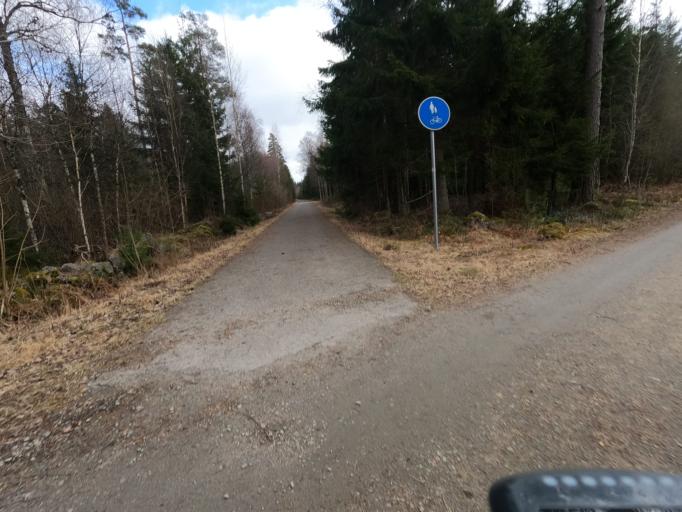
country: SE
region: Joenkoeping
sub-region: Varnamo Kommun
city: Rydaholm
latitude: 56.8537
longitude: 14.1890
